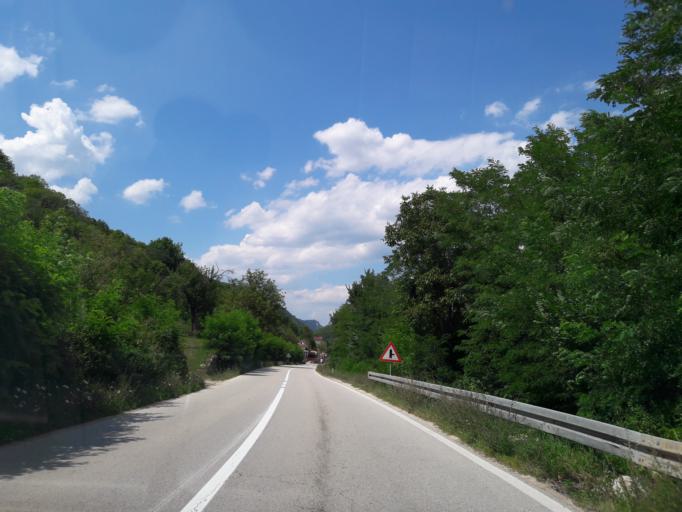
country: BA
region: Republika Srpska
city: Mrkonjic Grad
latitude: 44.5338
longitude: 17.1501
